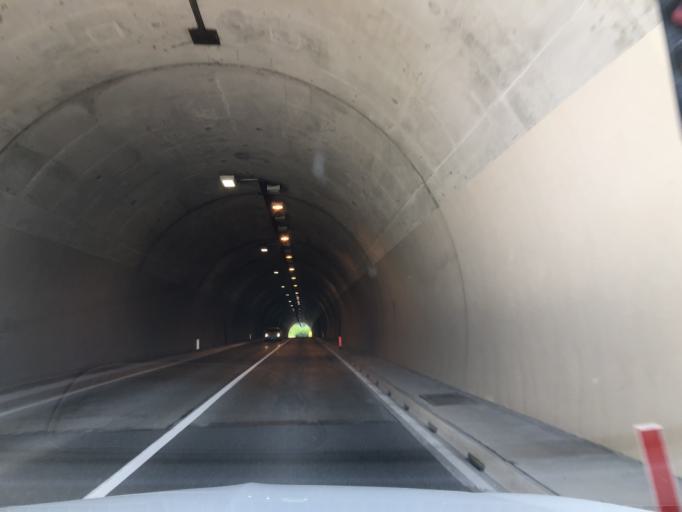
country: SI
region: Nova Gorica
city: Solkan
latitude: 45.9698
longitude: 13.6521
